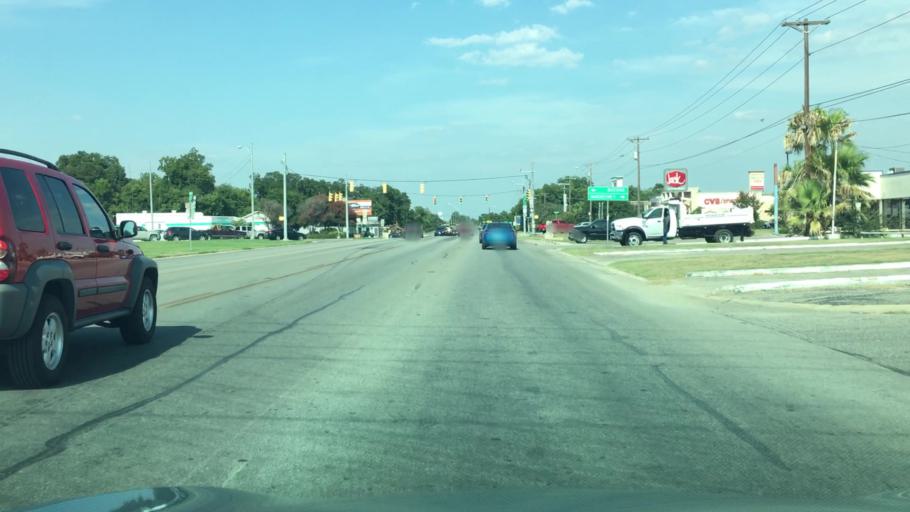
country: US
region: Texas
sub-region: Comal County
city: New Braunfels
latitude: 29.6936
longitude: -98.1125
